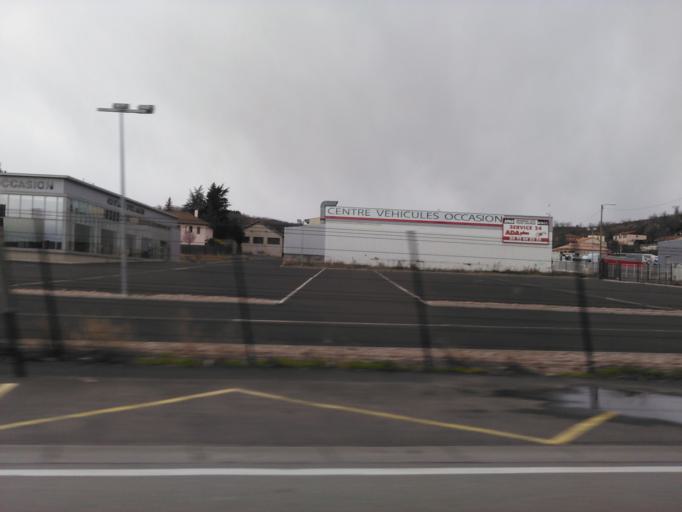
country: FR
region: Auvergne
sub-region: Departement du Puy-de-Dome
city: Perignat-les-Sarlieve
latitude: 45.7488
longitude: 3.1345
